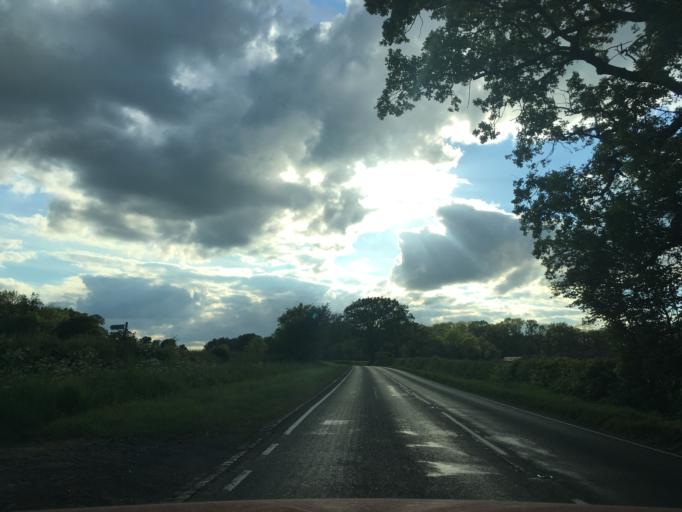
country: GB
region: England
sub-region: Worcestershire
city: Droitwich
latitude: 52.1859
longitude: -2.1220
